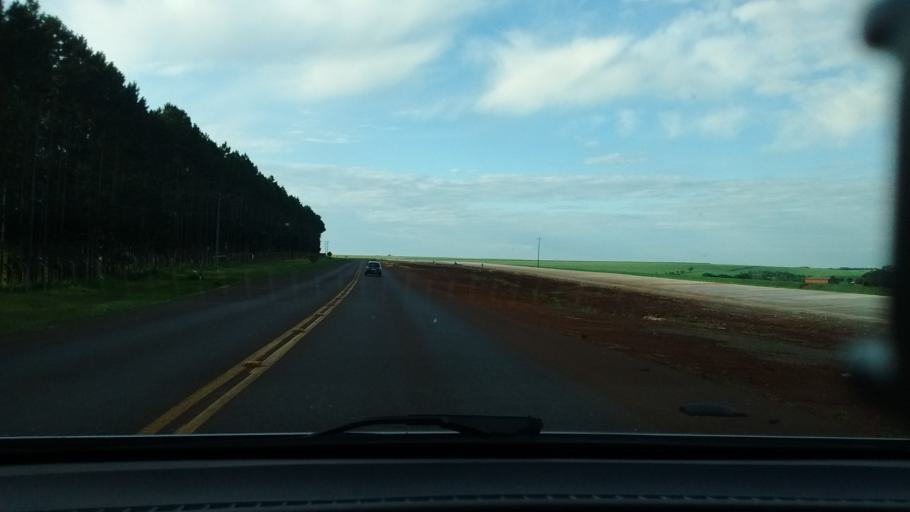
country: BR
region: Parana
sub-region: Cascavel
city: Cascavel
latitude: -25.0900
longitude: -53.5930
